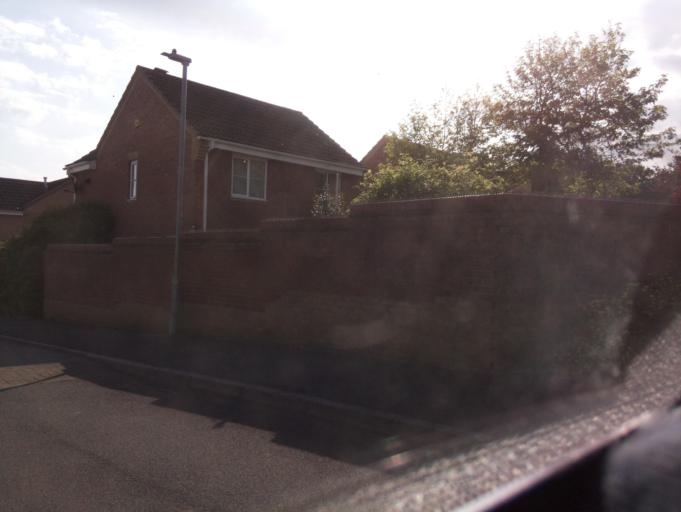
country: GB
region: England
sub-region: Wiltshire
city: Chippenham
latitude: 51.4693
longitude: -2.1113
